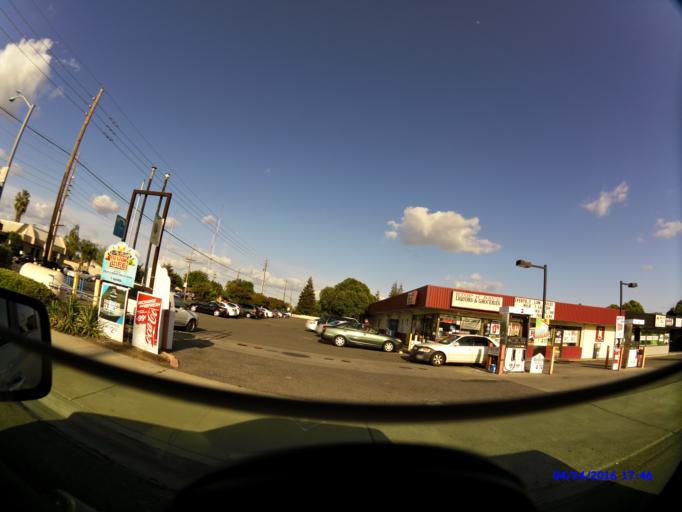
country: US
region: California
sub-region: Stanislaus County
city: Riverbank
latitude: 37.6887
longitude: -120.9579
